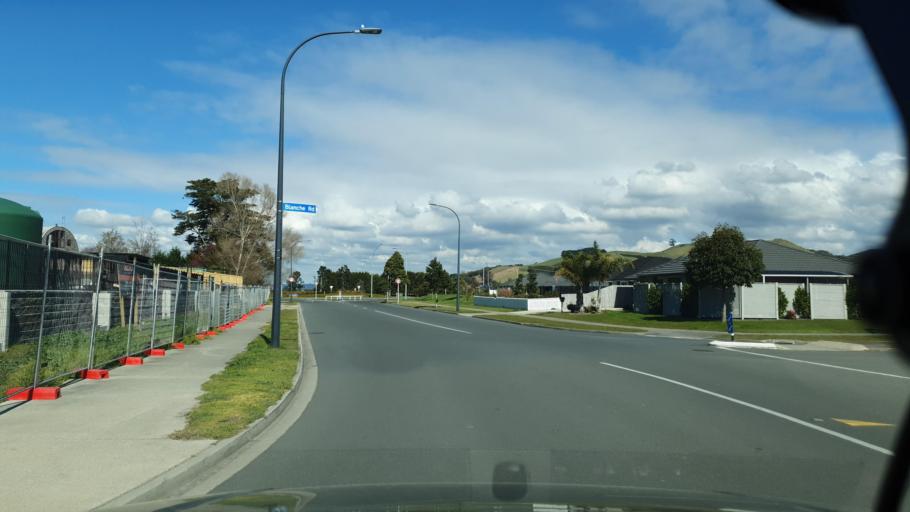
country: NZ
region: Bay of Plenty
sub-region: Tauranga City
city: Tauranga
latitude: -37.7129
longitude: 176.3001
